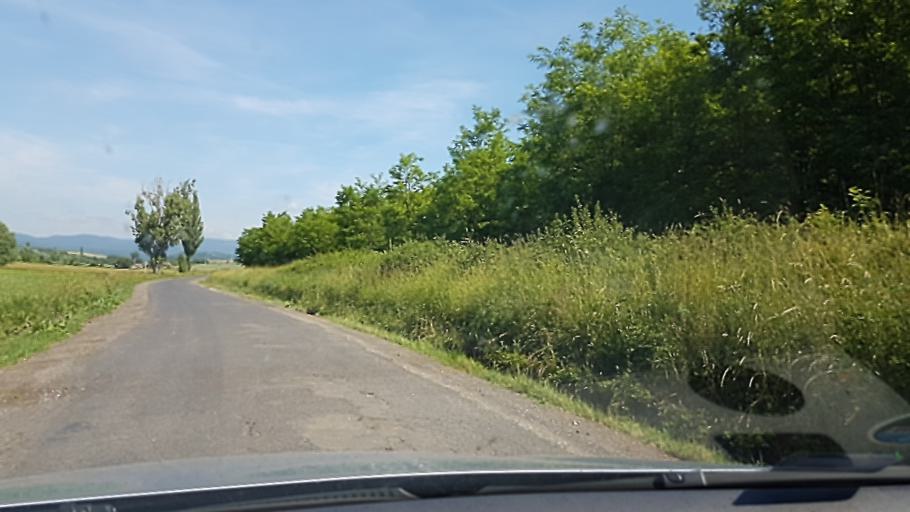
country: HU
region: Borsod-Abauj-Zemplen
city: Saly
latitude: 47.9423
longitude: 20.7064
